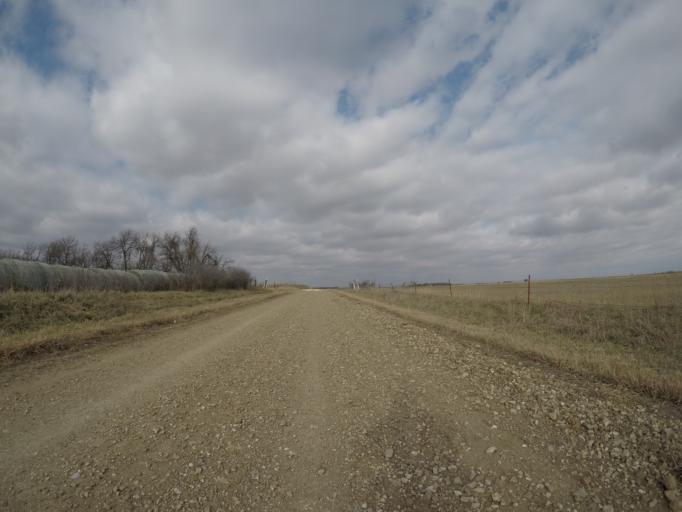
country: US
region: Kansas
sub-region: Morris County
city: Council Grove
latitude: 38.7895
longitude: -96.3527
